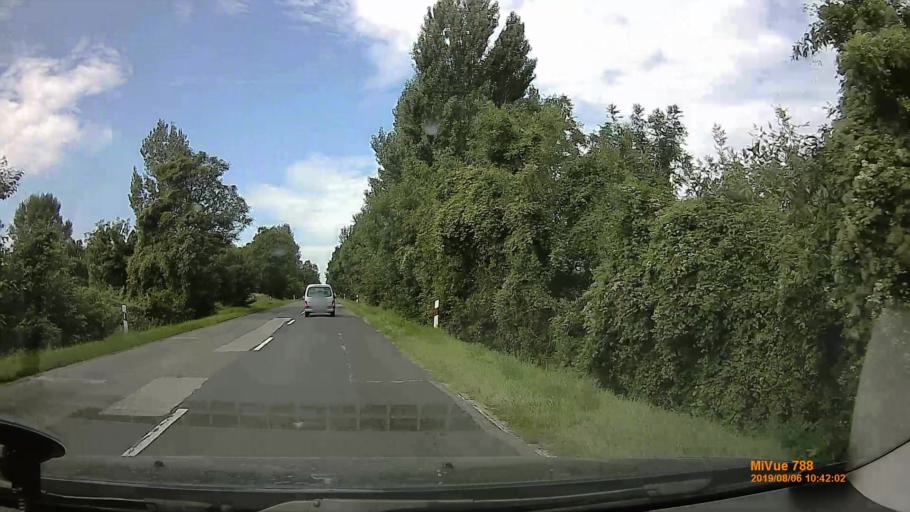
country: HU
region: Zala
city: Zalakomar
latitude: 46.5132
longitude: 17.1291
